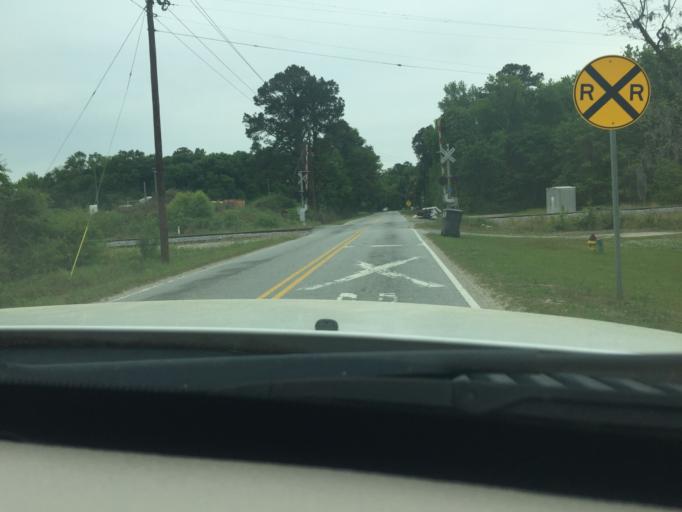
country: US
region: Georgia
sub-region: Chatham County
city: Georgetown
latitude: 31.9757
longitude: -81.2479
